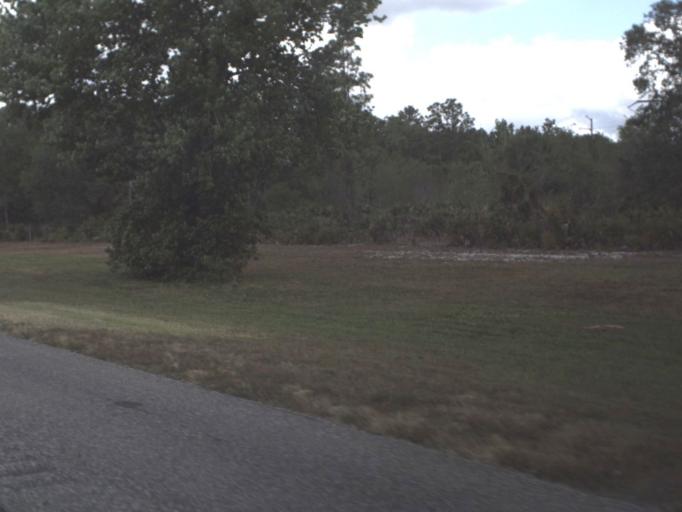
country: US
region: Florida
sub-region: Orange County
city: Wedgefield
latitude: 28.4526
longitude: -81.0127
